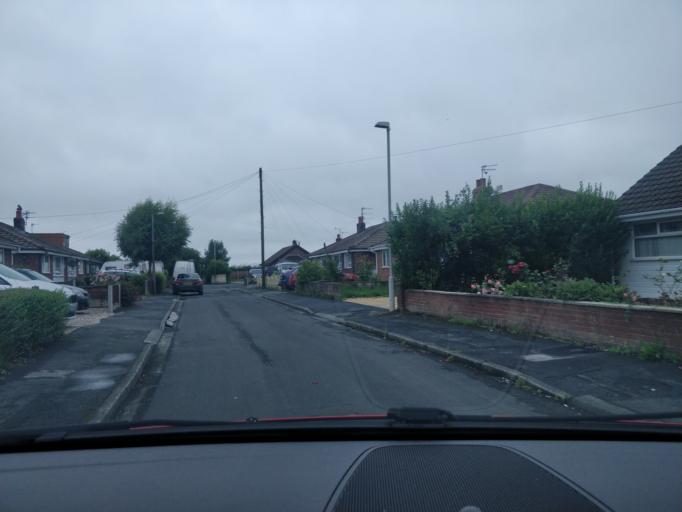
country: GB
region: England
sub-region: Lancashire
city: Banks
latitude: 53.6758
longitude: -2.9334
